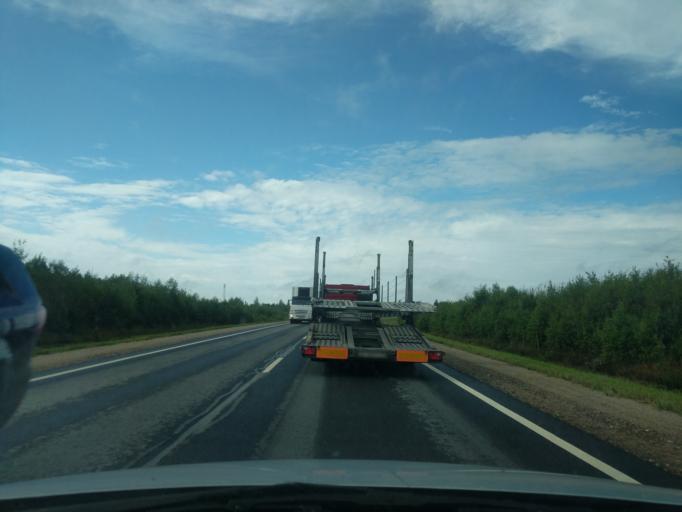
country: RU
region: Kostroma
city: Sudislavl'
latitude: 57.8214
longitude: 41.9083
